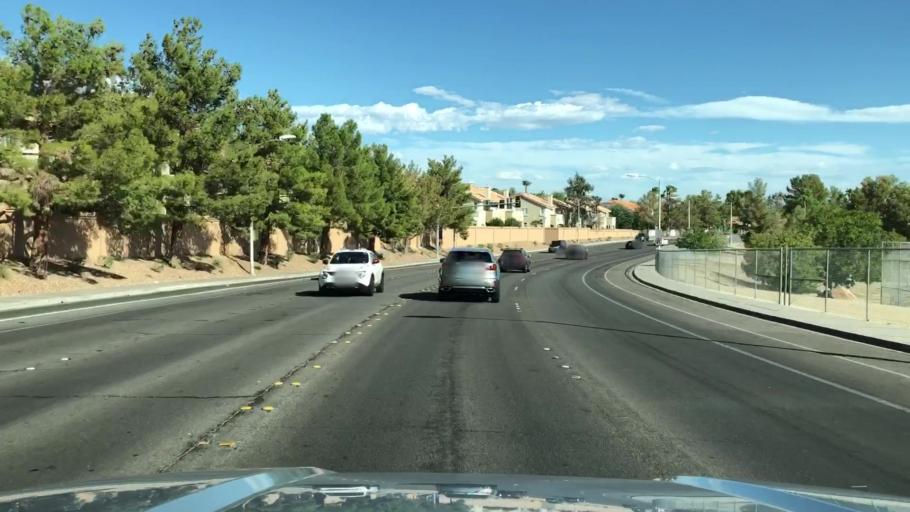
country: US
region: Nevada
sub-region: Clark County
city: Whitney
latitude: 36.0363
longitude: -115.0681
